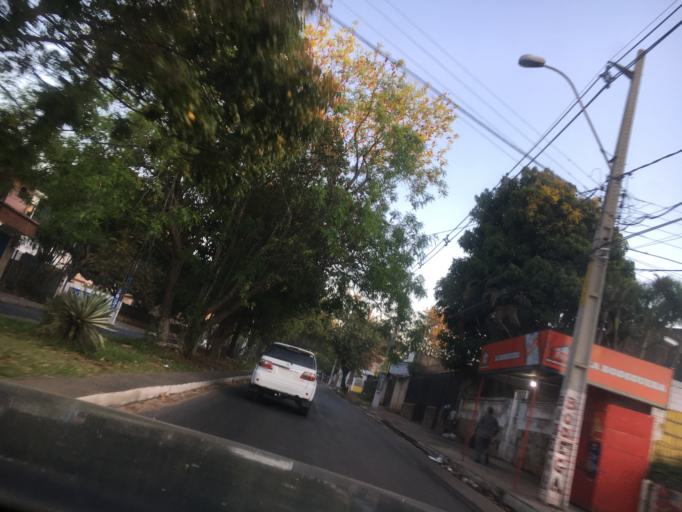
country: PY
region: Central
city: Lambare
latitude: -25.3360
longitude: -57.6068
